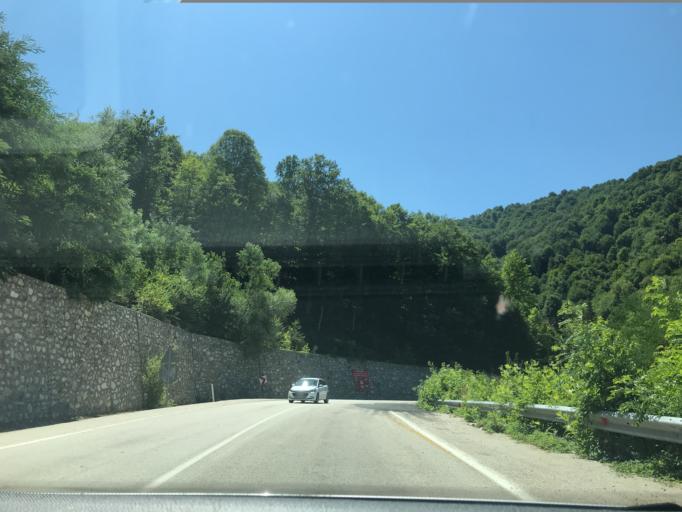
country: TR
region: Bursa
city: Tahtakopru
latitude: 39.9290
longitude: 29.5879
